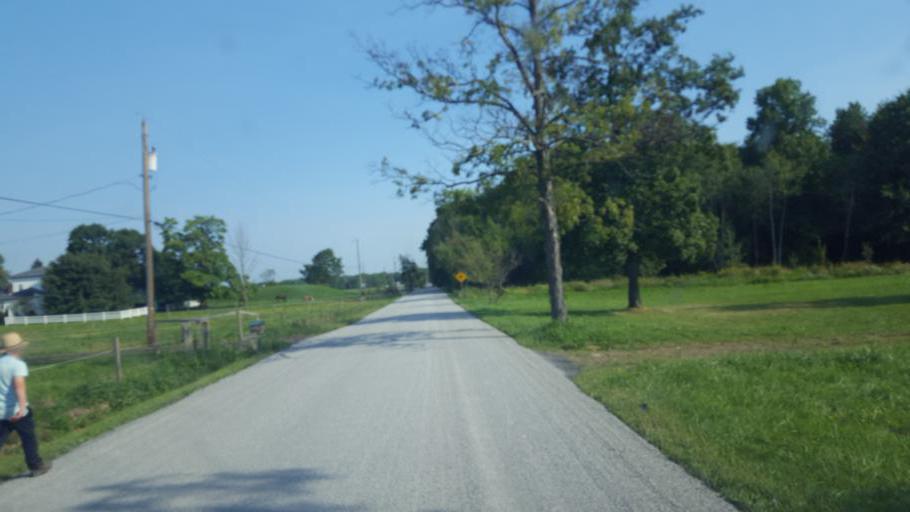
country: US
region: Ohio
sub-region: Geauga County
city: Middlefield
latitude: 41.4730
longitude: -80.9745
